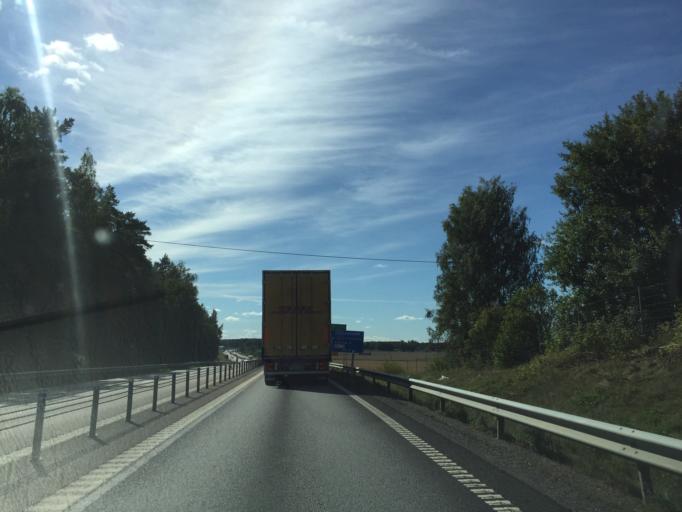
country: SE
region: Vaestmanland
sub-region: Kopings Kommun
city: Koping
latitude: 59.5324
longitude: 15.9856
